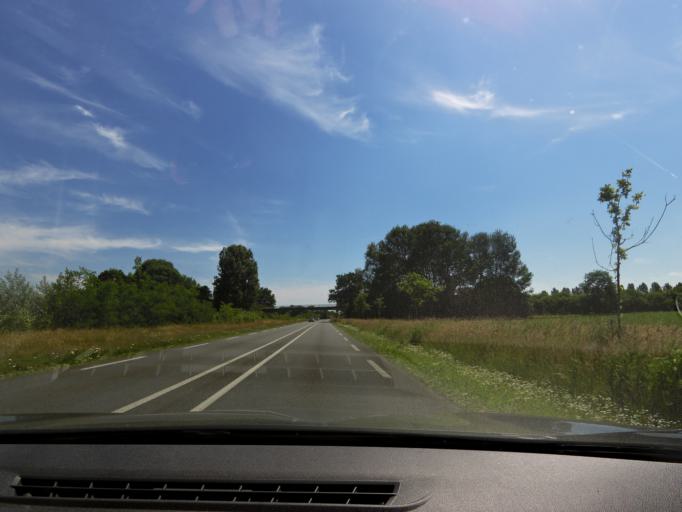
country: NL
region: Overijssel
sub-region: Gemeente Wierden
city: Wierden
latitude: 52.3136
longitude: 6.5486
